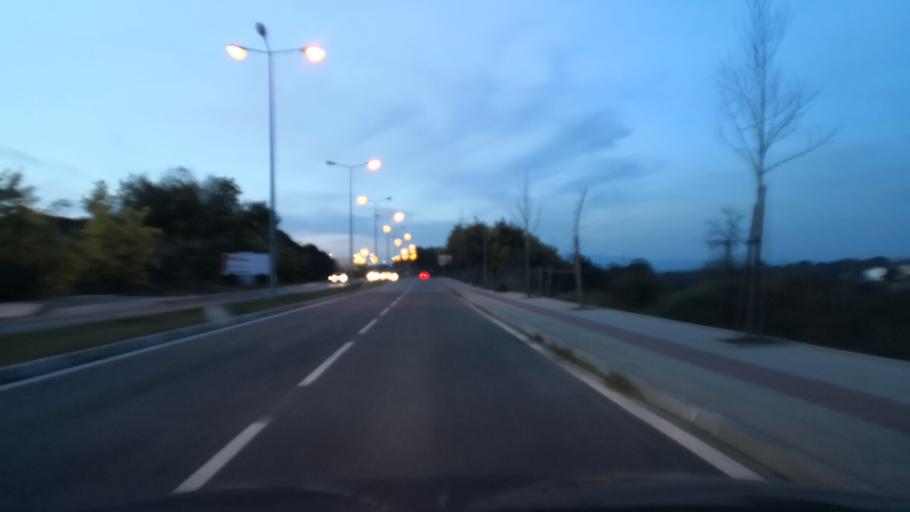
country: PT
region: Castelo Branco
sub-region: Castelo Branco
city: Castelo Branco
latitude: 39.8287
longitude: -7.4858
